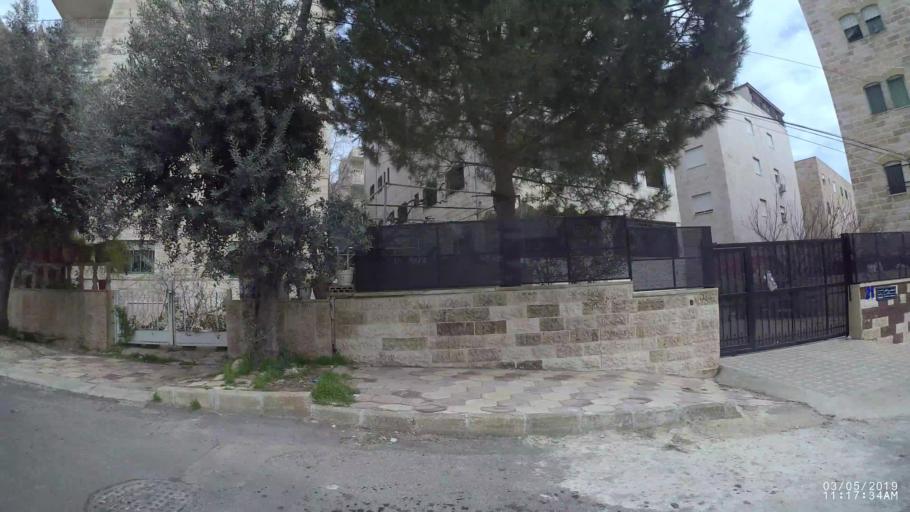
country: JO
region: Amman
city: Amman
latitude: 31.9909
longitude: 35.9264
